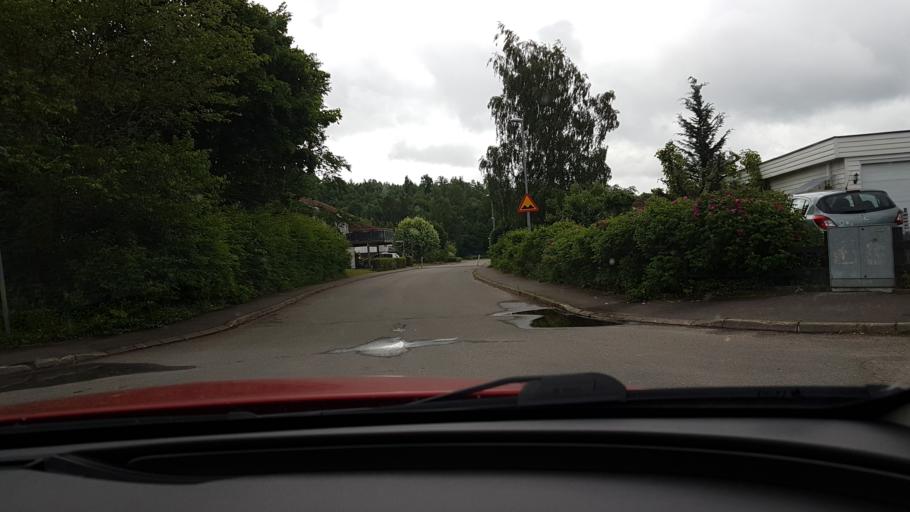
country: SE
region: Vaestra Goetaland
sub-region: Skovde Kommun
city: Skultorp
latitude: 58.3660
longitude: 13.8248
